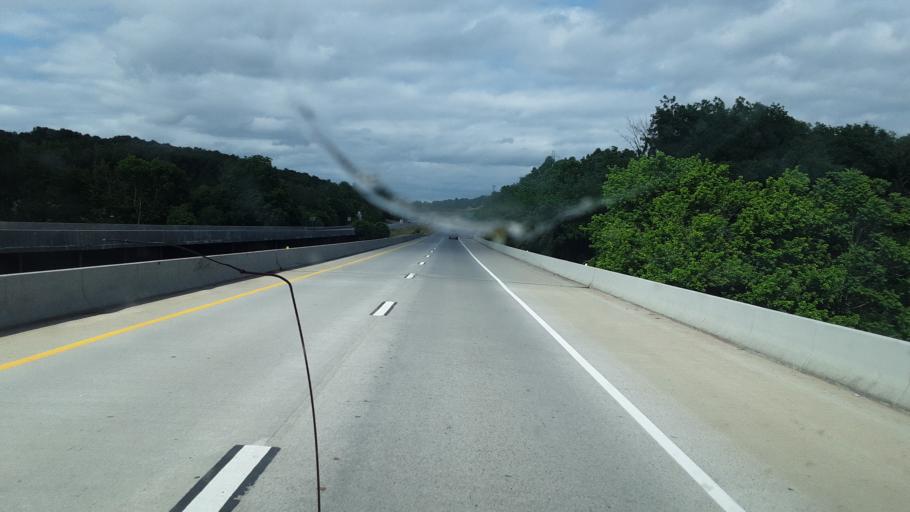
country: US
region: Virginia
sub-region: City of Danville
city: Danville
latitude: 36.5696
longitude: -79.3733
